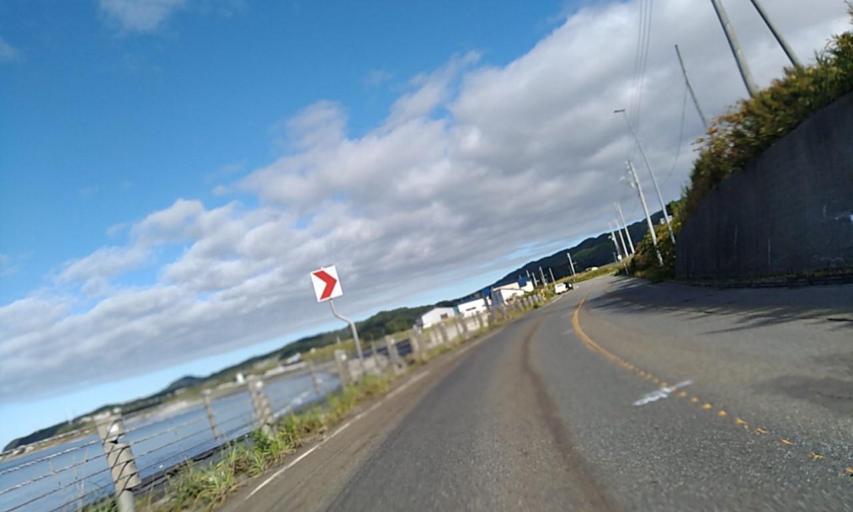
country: JP
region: Hokkaido
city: Shizunai-furukawacho
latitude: 42.2401
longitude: 142.5895
